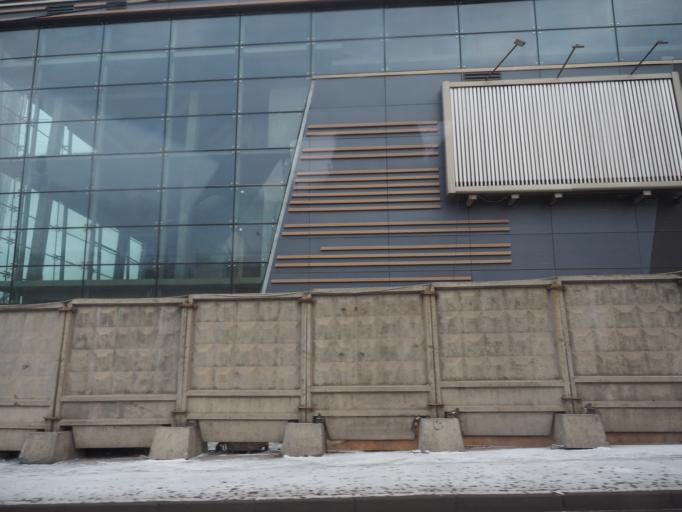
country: RU
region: Moskovskaya
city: Kastanayevo
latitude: 55.7150
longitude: 37.5037
